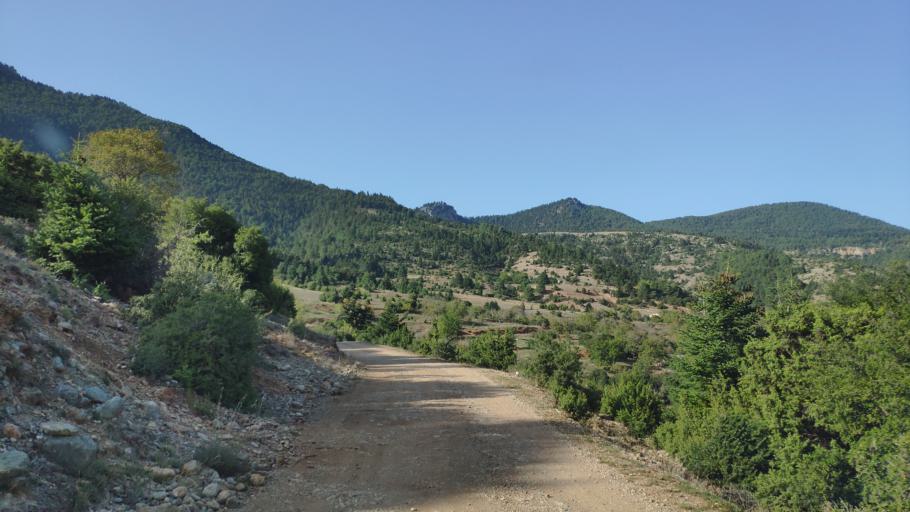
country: GR
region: West Greece
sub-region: Nomos Achaias
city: Aiyira
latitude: 37.9871
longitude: 22.3485
